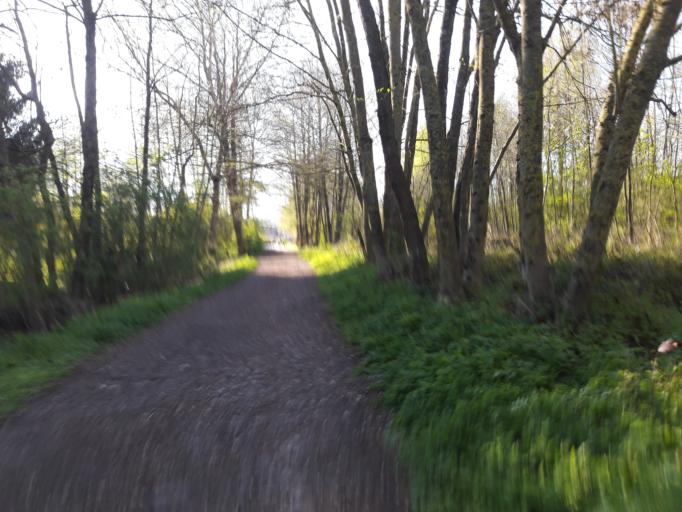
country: FR
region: Nord-Pas-de-Calais
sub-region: Departement du Nord
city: Ferriere-la-Grande
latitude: 50.2540
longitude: 4.0023
